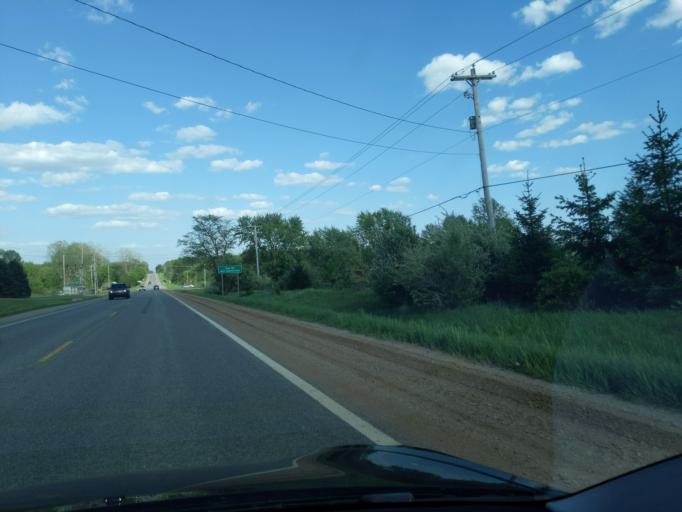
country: US
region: Michigan
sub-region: Ionia County
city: Portland
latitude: 42.7556
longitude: -84.9628
